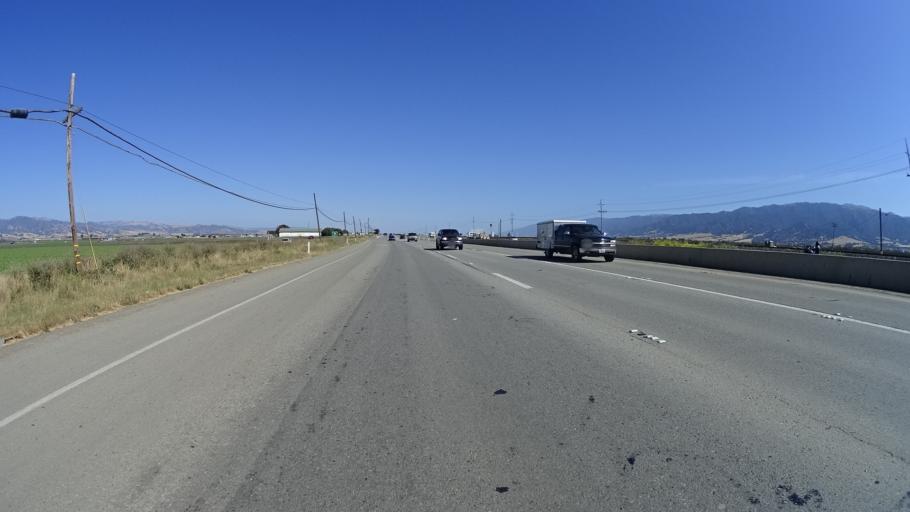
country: US
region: California
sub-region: Monterey County
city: Chualar
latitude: 36.6237
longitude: -121.5819
